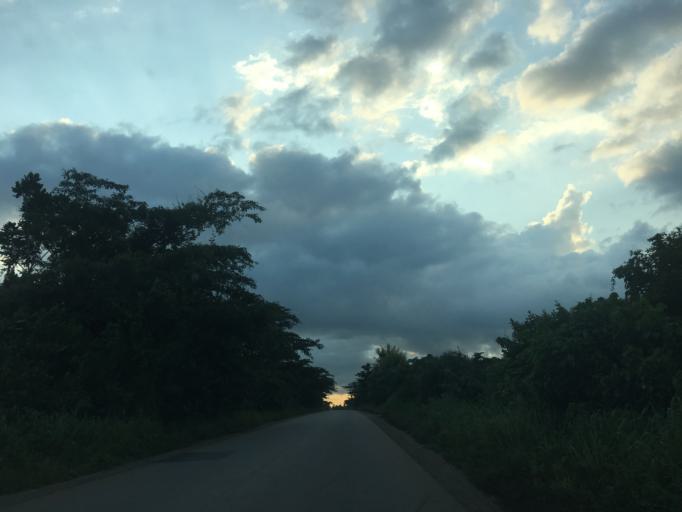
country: GH
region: Western
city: Bibiani
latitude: 6.7155
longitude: -2.4615
